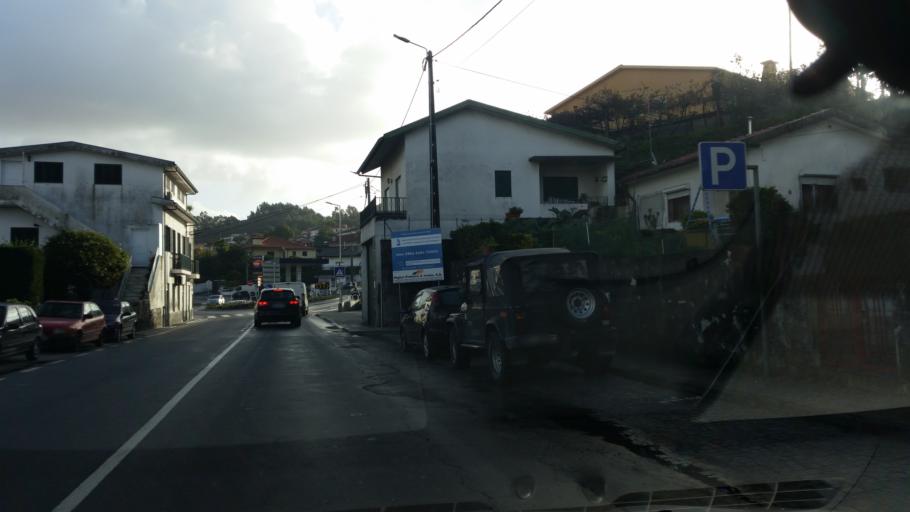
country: PT
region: Porto
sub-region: Santo Tirso
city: Negrelos
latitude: 41.3549
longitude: -8.4081
